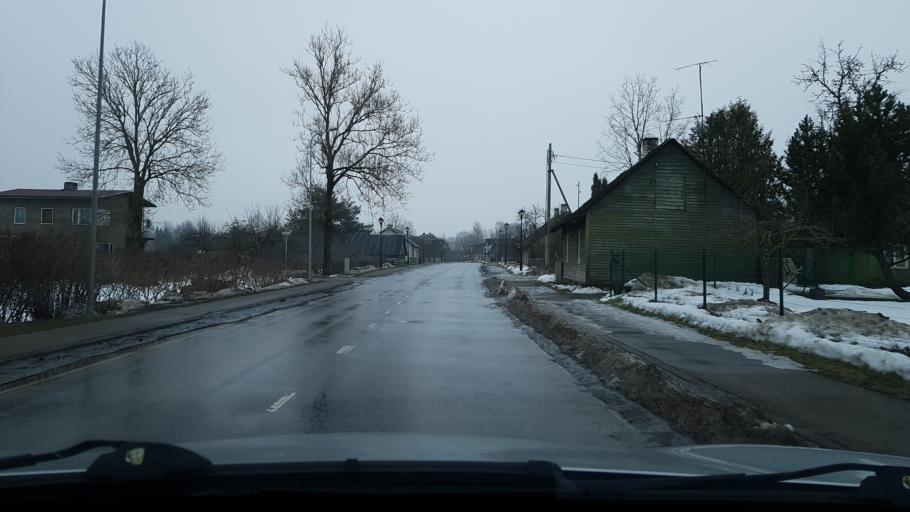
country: EE
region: Valgamaa
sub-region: Torva linn
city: Torva
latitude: 58.2392
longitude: 25.8582
